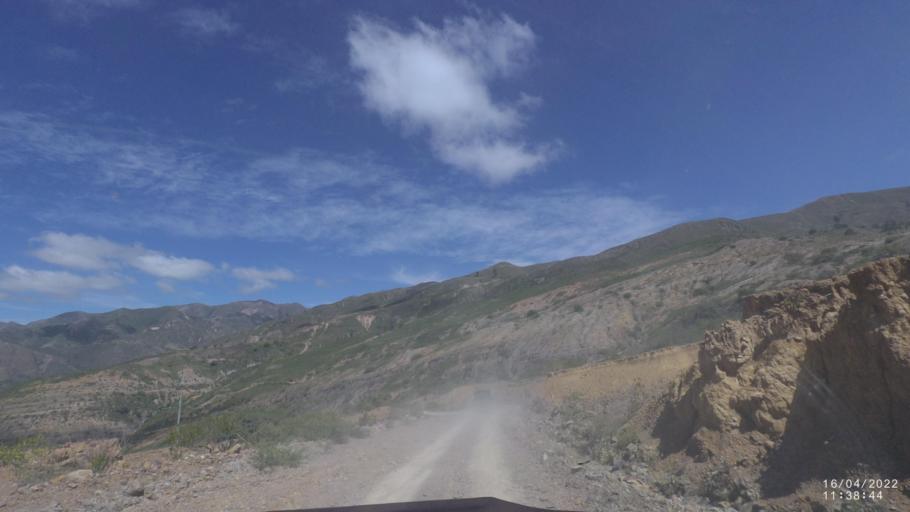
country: BO
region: Cochabamba
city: Mizque
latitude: -17.9647
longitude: -65.6375
